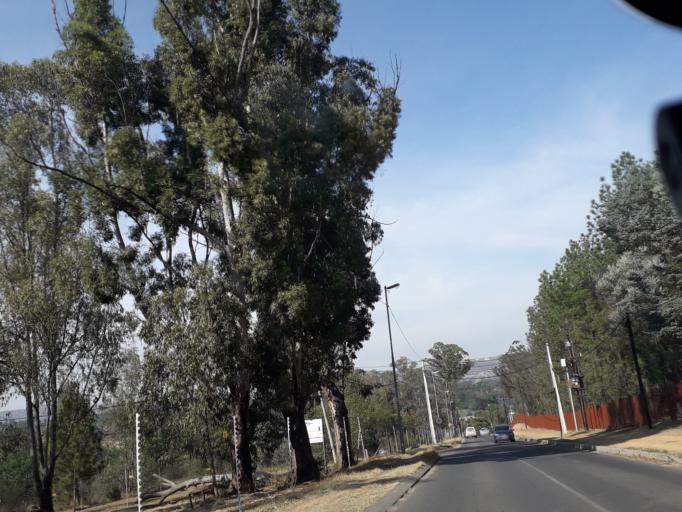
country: ZA
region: Gauteng
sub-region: West Rand District Municipality
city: Muldersdriseloop
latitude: -26.0727
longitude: 27.8959
